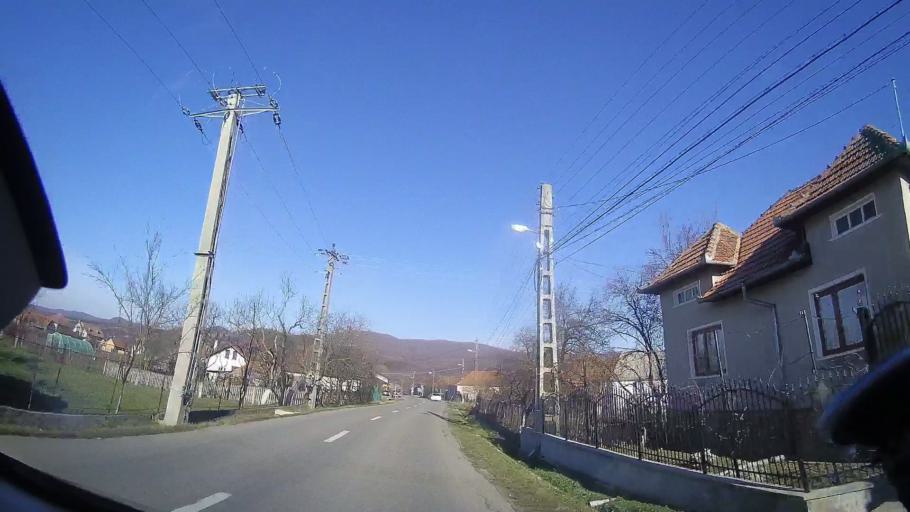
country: RO
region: Bihor
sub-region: Comuna Borod
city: Borod
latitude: 46.9894
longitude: 22.6173
